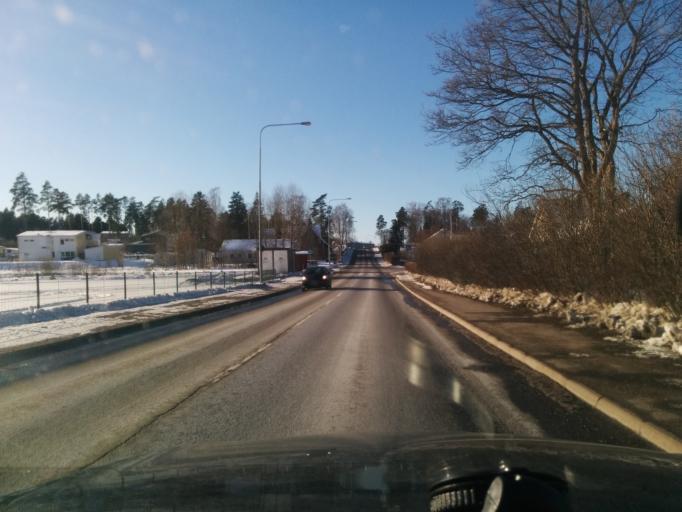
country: SE
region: Stockholm
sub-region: Vallentuna Kommun
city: Vallentuna
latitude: 59.4974
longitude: 18.0844
